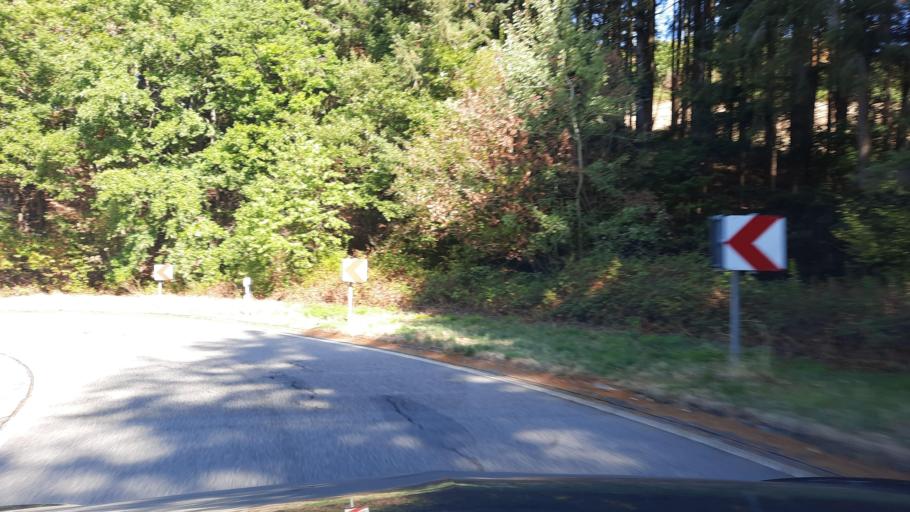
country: DE
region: Rheinland-Pfalz
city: Irsch
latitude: 49.5960
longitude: 6.5948
